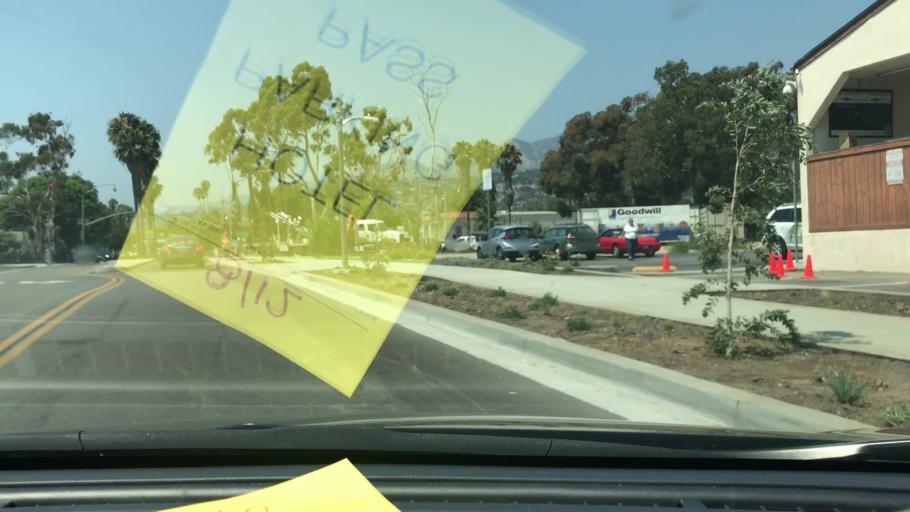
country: US
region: California
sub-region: Santa Barbara County
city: Santa Barbara
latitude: 34.4180
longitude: -119.6739
